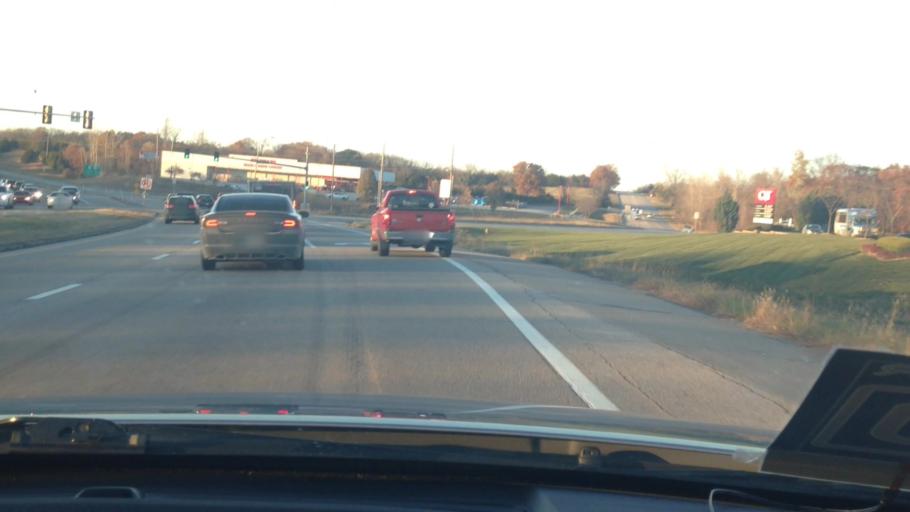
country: US
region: Kansas
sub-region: Wyandotte County
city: Bonner Springs
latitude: 39.1035
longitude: -94.8807
